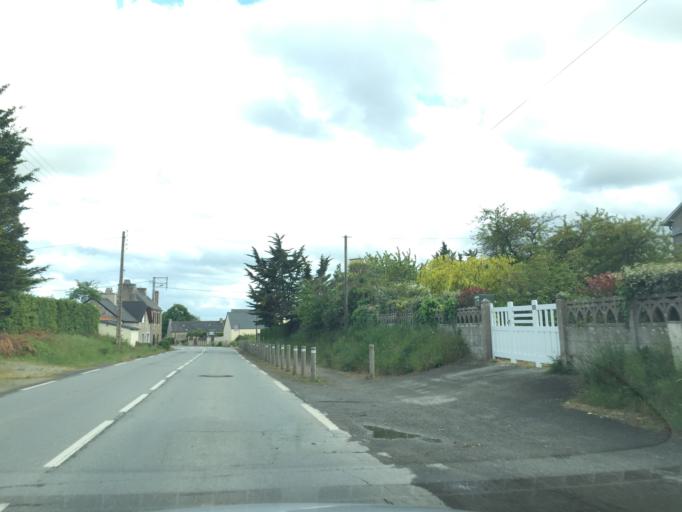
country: FR
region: Brittany
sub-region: Departement des Cotes-d'Armor
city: Lancieux
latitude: 48.5957
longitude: -2.1496
